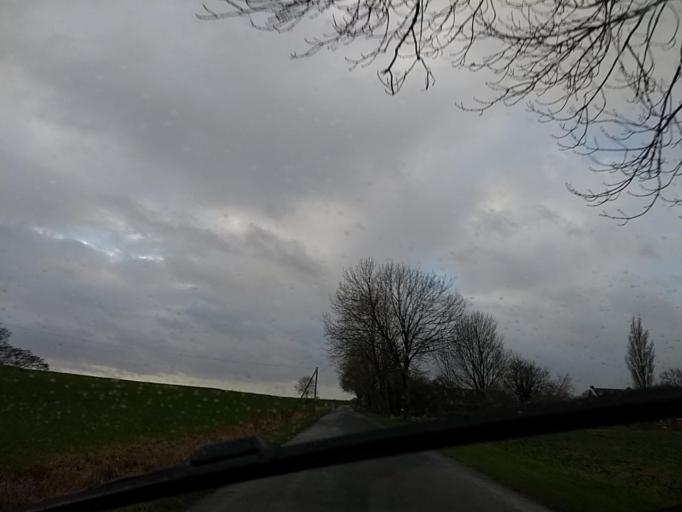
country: DE
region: Lower Saxony
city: Bunde
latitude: 53.2348
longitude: 7.2298
